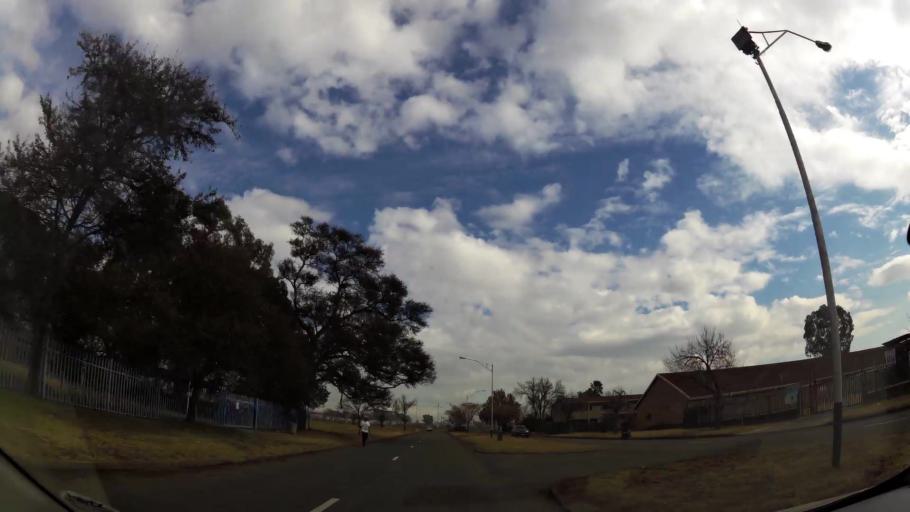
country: ZA
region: Gauteng
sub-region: Sedibeng District Municipality
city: Meyerton
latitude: -26.5589
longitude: 28.0119
